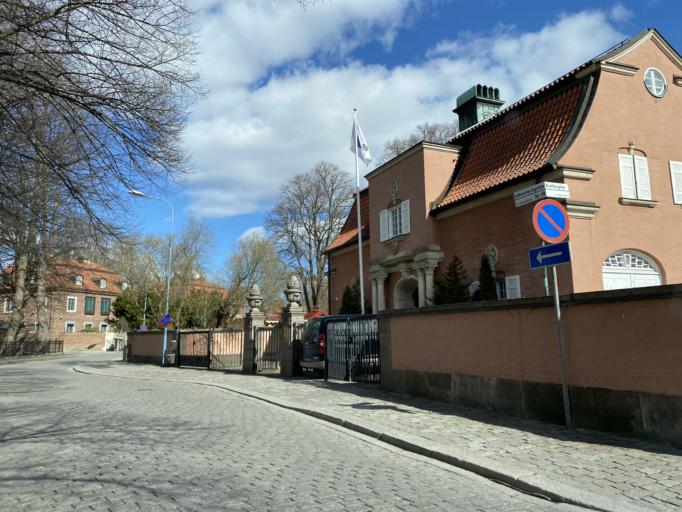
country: SE
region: Stockholm
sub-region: Stockholms Kommun
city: OEstermalm
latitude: 59.3324
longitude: 18.1026
